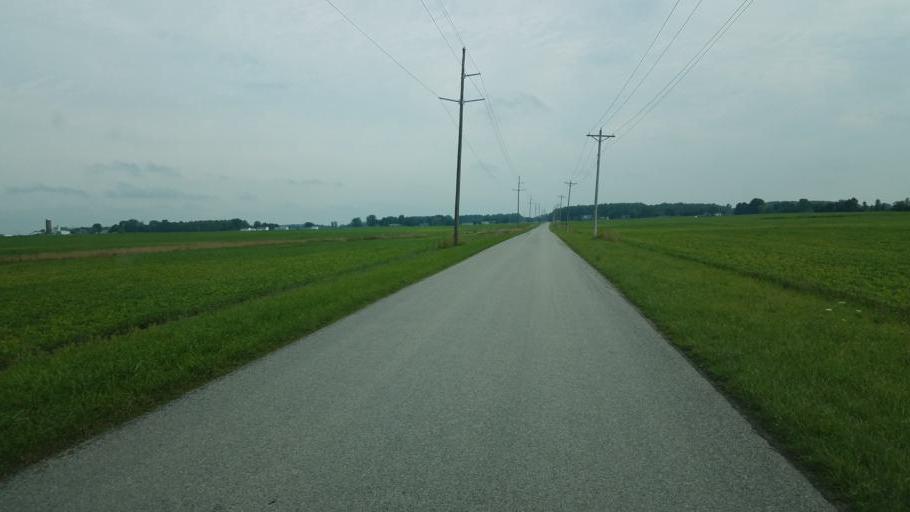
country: US
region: Ohio
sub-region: Delaware County
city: Ashley
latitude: 40.4126
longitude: -82.9101
